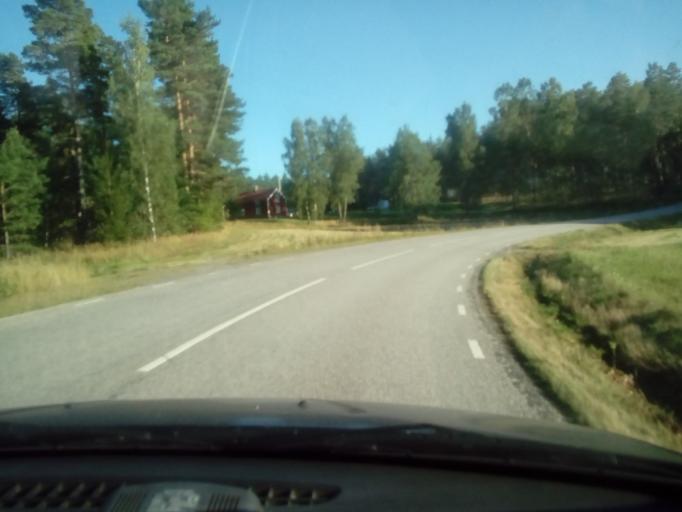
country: SE
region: Kalmar
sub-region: Vasterviks Kommun
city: Gamleby
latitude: 57.7959
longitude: 16.4142
